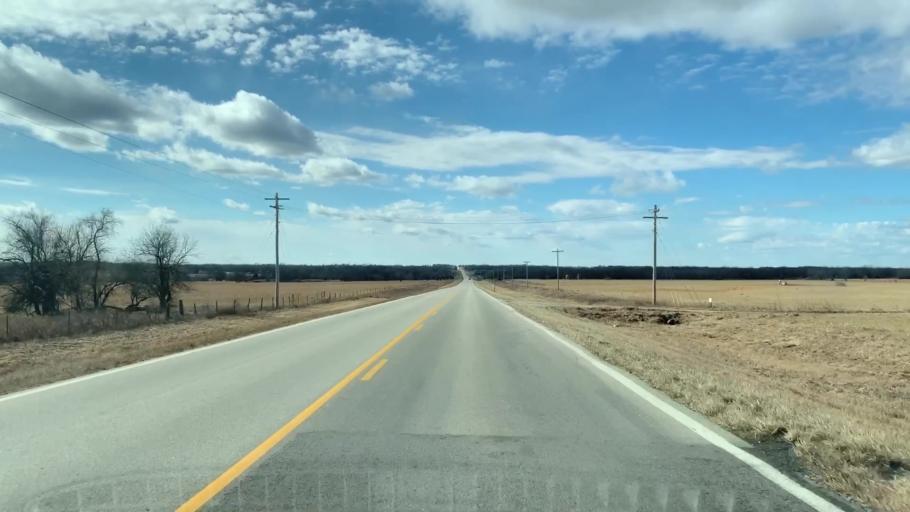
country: US
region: Kansas
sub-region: Neosho County
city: Erie
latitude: 37.5291
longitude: -95.3883
